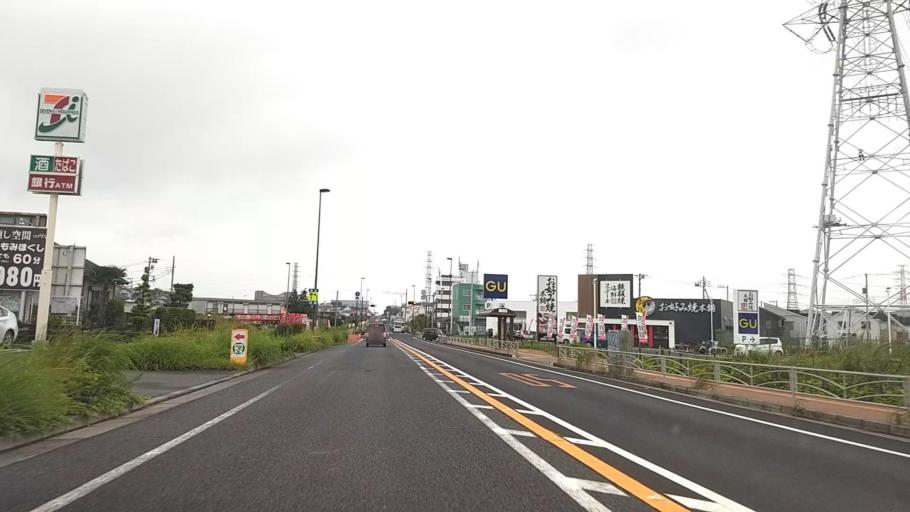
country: JP
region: Kanagawa
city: Isehara
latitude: 35.4093
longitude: 139.3256
